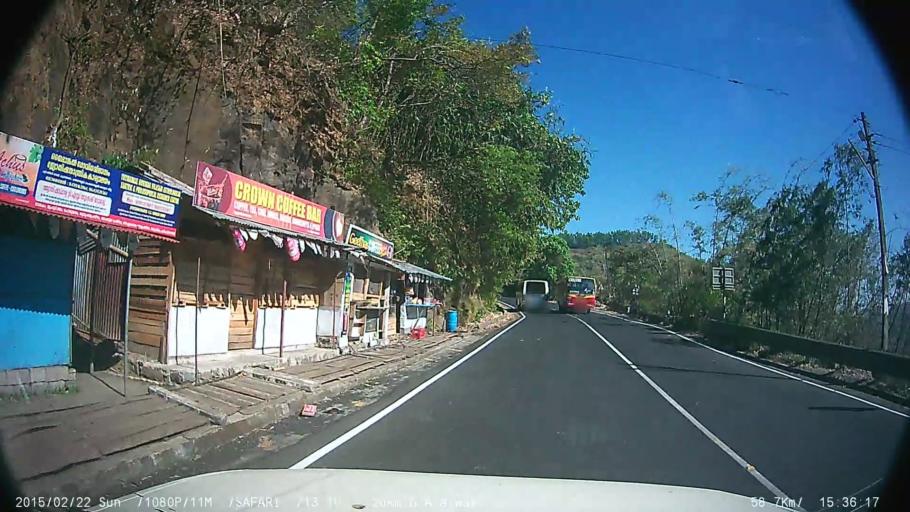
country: IN
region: Kerala
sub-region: Kottayam
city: Erattupetta
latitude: 9.5628
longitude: 76.9775
